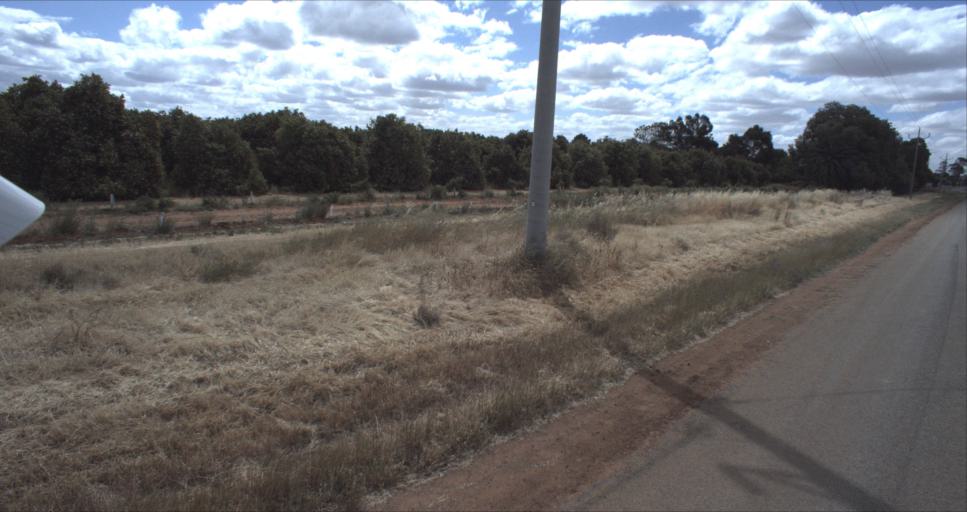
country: AU
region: New South Wales
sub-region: Leeton
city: Leeton
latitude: -34.5837
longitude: 146.3965
